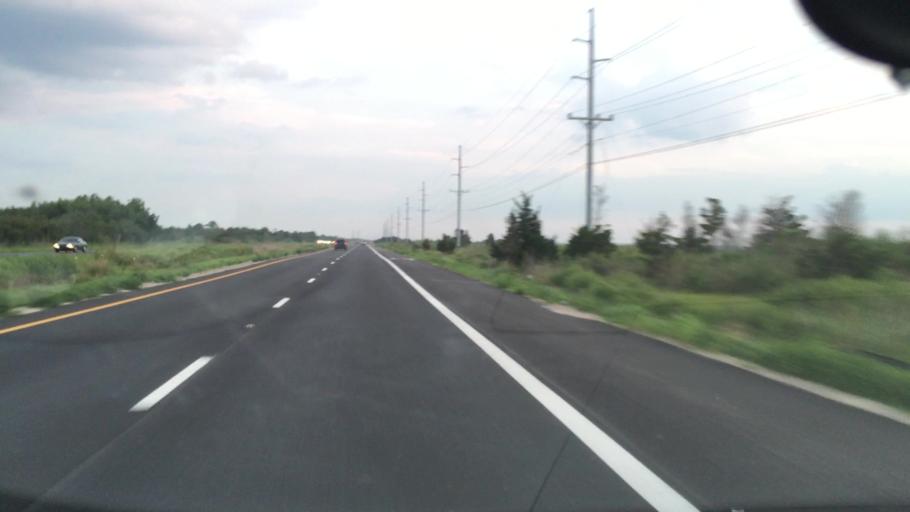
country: US
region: Delaware
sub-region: Sussex County
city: Rehoboth Beach
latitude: 38.6595
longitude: -75.0700
